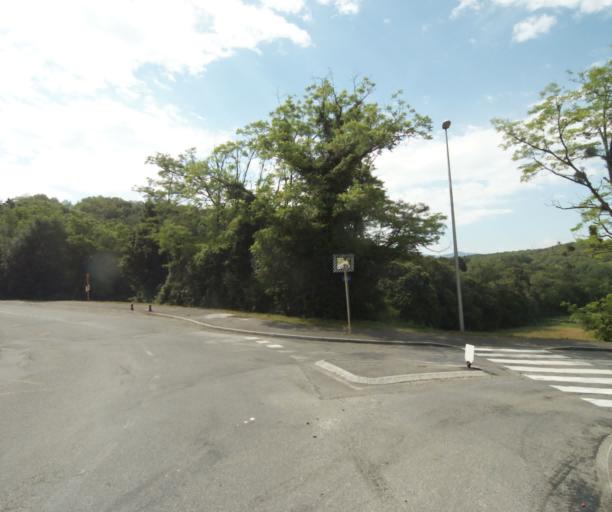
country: FR
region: Rhone-Alpes
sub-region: Departement de la Haute-Savoie
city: Thonon-les-Bains
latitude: 46.3590
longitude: 6.4965
